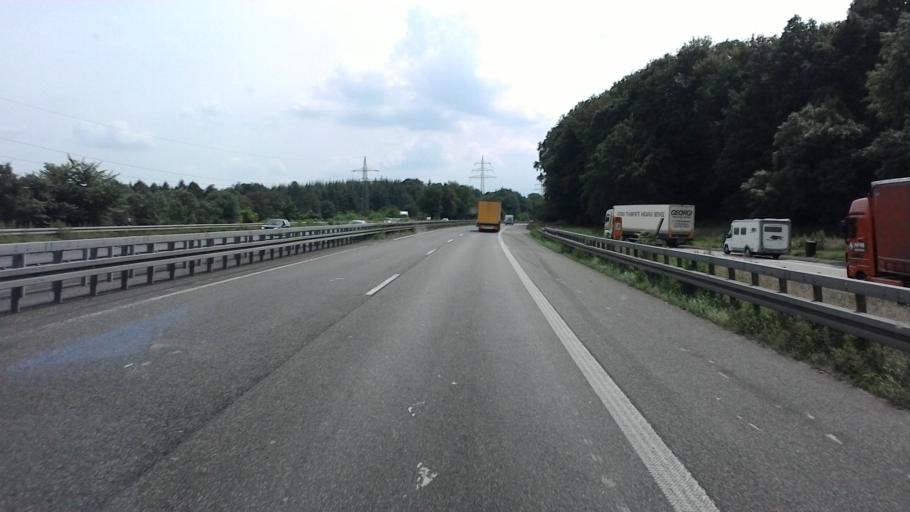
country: DE
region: North Rhine-Westphalia
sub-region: Regierungsbezirk Koln
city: Wurselen
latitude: 50.7855
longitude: 6.1745
